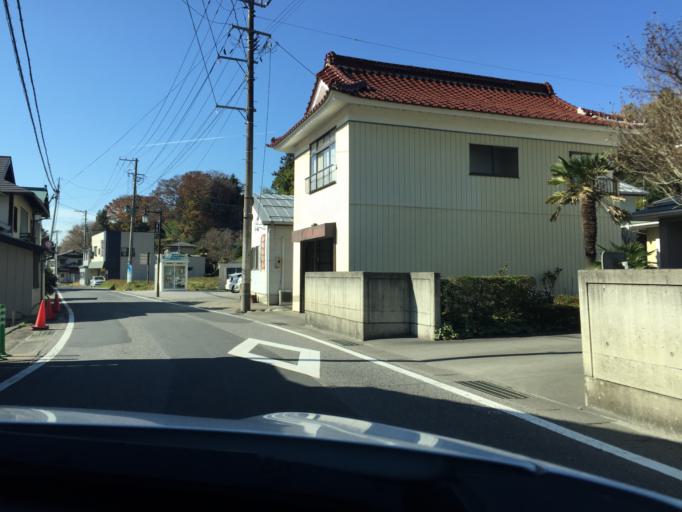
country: JP
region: Fukushima
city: Miharu
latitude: 37.3638
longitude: 140.5232
